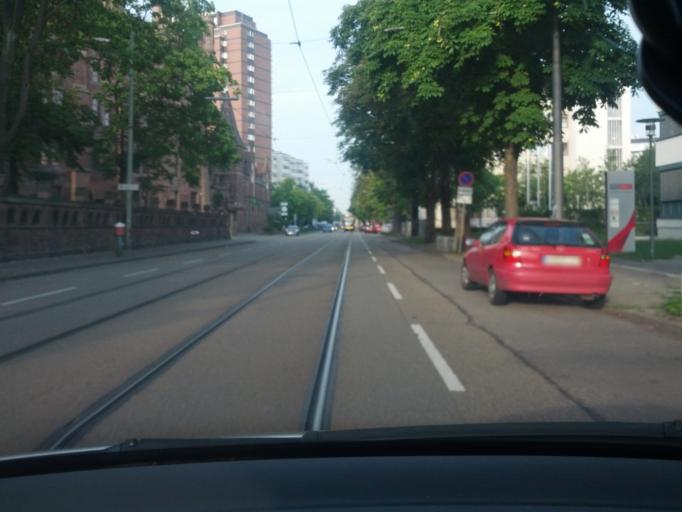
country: DE
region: Baden-Wuerttemberg
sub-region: Karlsruhe Region
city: Karlsruhe
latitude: 49.0131
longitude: 8.4277
